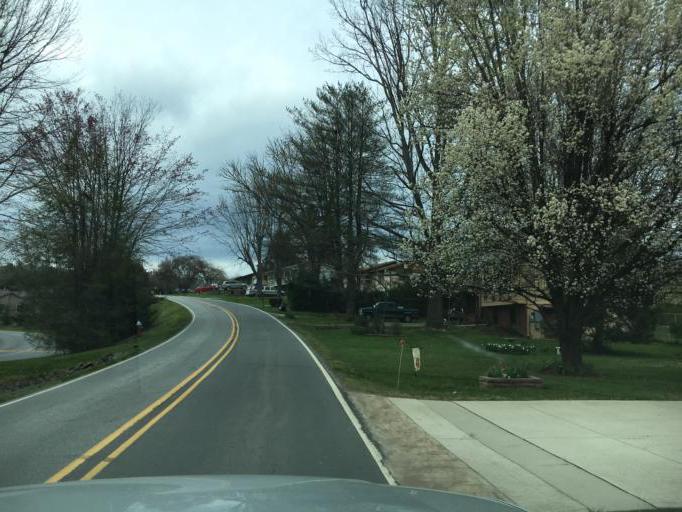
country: US
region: North Carolina
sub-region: Transylvania County
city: Brevard
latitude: 35.2397
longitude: -82.7203
